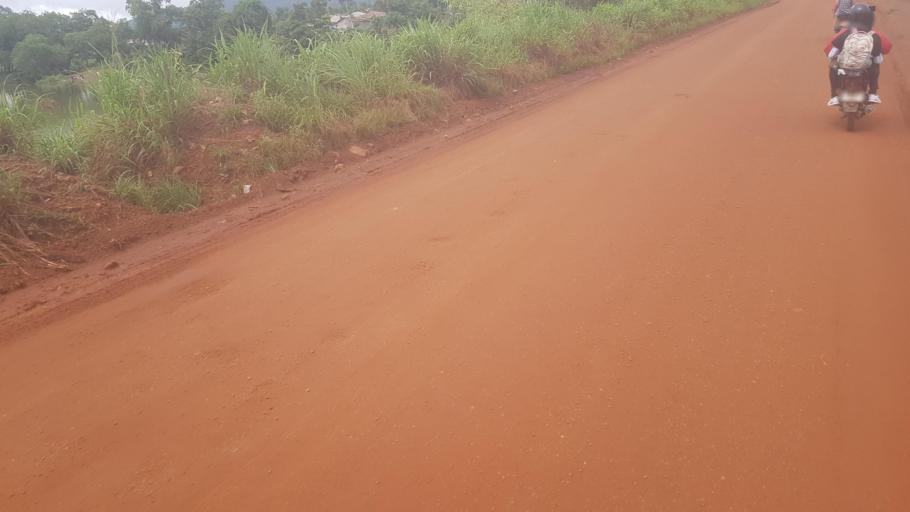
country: SL
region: Southern Province
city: Mogbwemo
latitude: 7.7644
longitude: -12.3037
